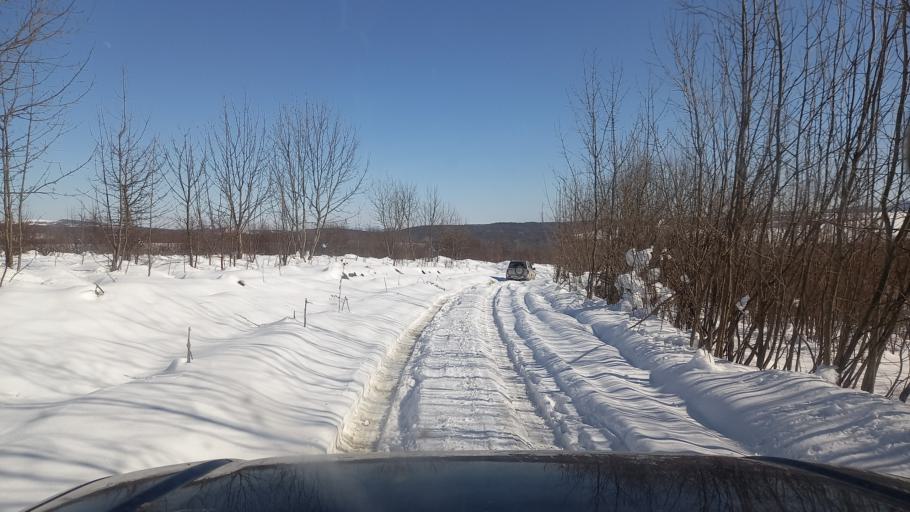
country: RU
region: Krasnodarskiy
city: Gubskaya
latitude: 44.3393
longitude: 40.4412
